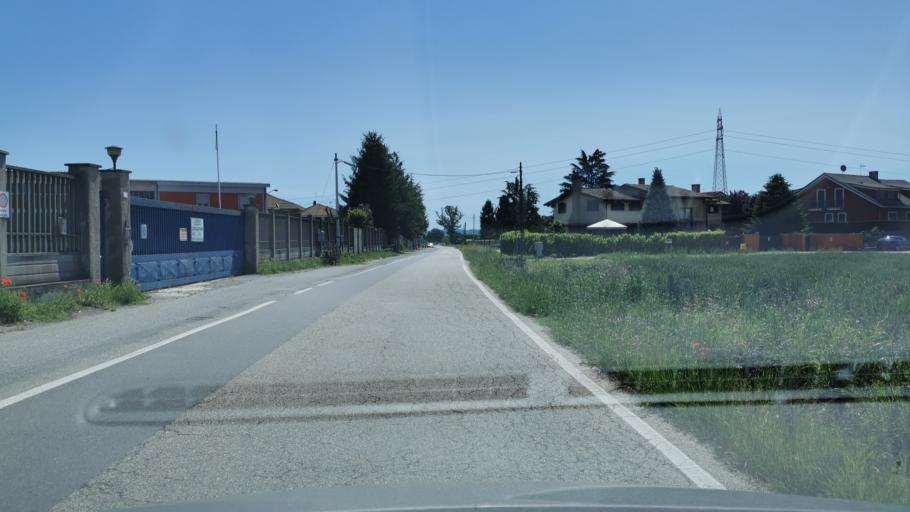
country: IT
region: Piedmont
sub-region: Provincia di Torino
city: Leini
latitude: 45.1743
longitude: 7.7230
